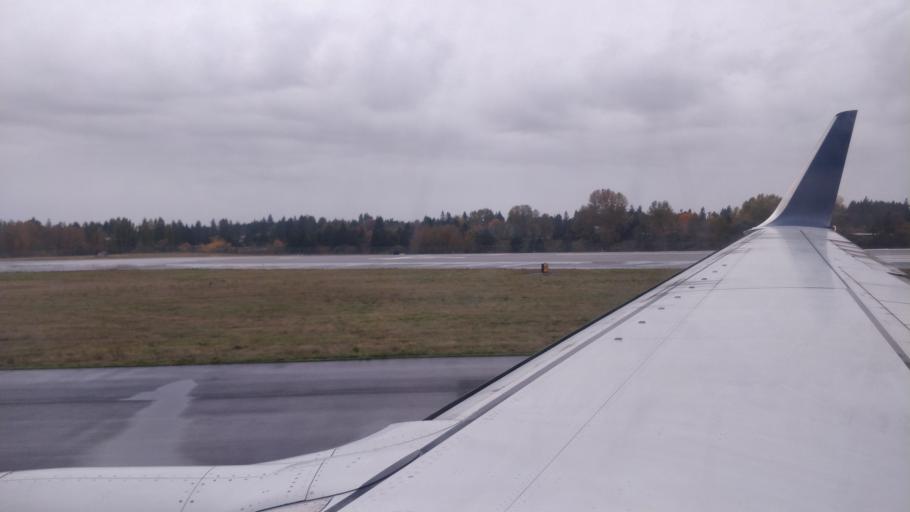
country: US
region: Washington
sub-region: King County
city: Normandy Park
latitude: 47.4421
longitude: -122.3166
